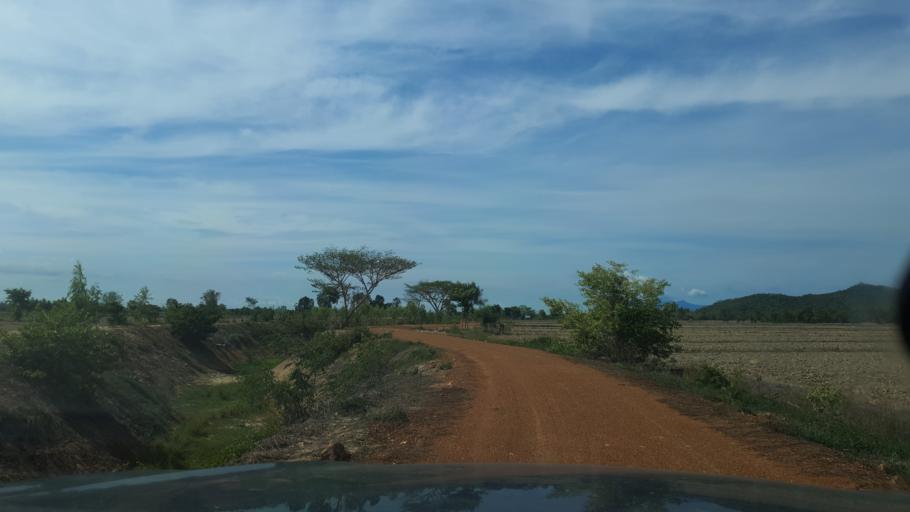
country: TH
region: Sukhothai
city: Thung Saliam
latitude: 17.2535
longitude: 99.6620
